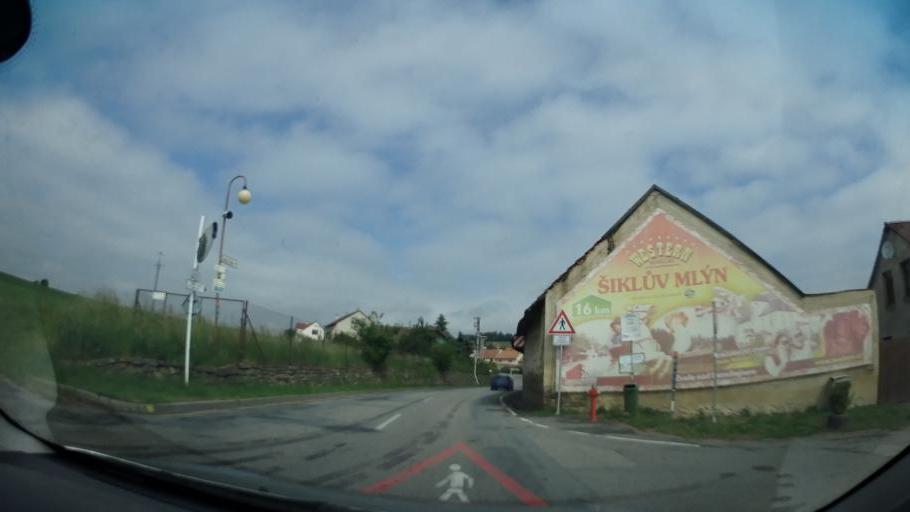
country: CZ
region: South Moravian
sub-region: Okres Brno-Venkov
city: Dolni Loucky
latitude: 49.3778
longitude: 16.3529
